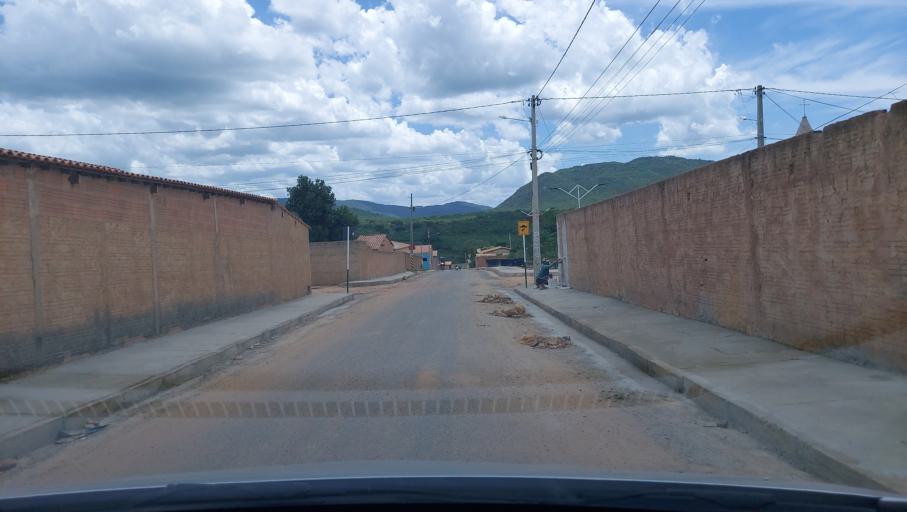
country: BR
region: Bahia
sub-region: Oliveira Dos Brejinhos
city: Beira Rio
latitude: -12.0060
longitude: -42.6301
